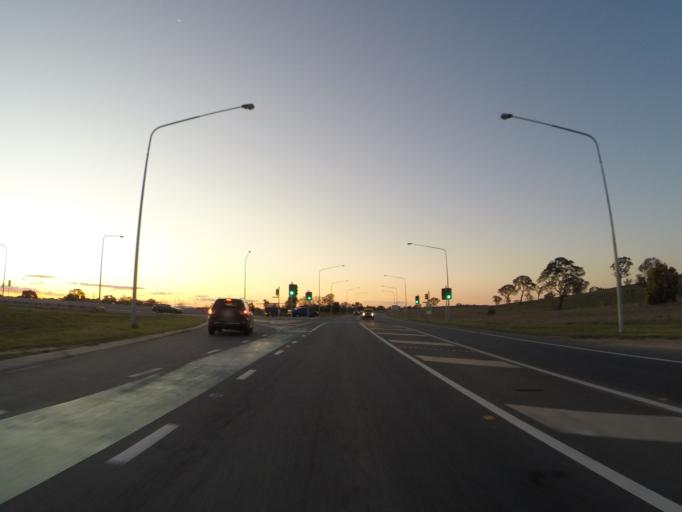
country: AU
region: Australian Capital Territory
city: Kaleen
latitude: -35.2007
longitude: 149.1658
